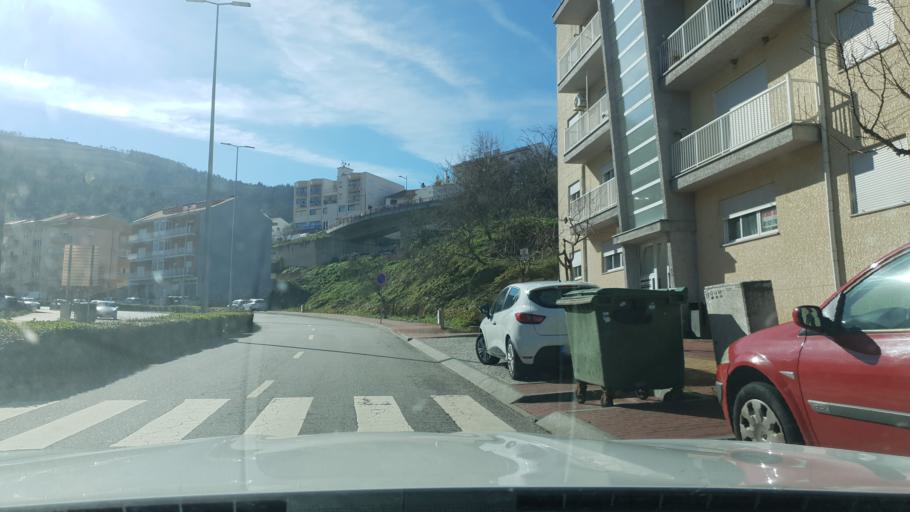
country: PT
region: Braganca
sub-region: Torre de Moncorvo
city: Torre de Moncorvo
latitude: 41.1759
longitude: -7.0503
